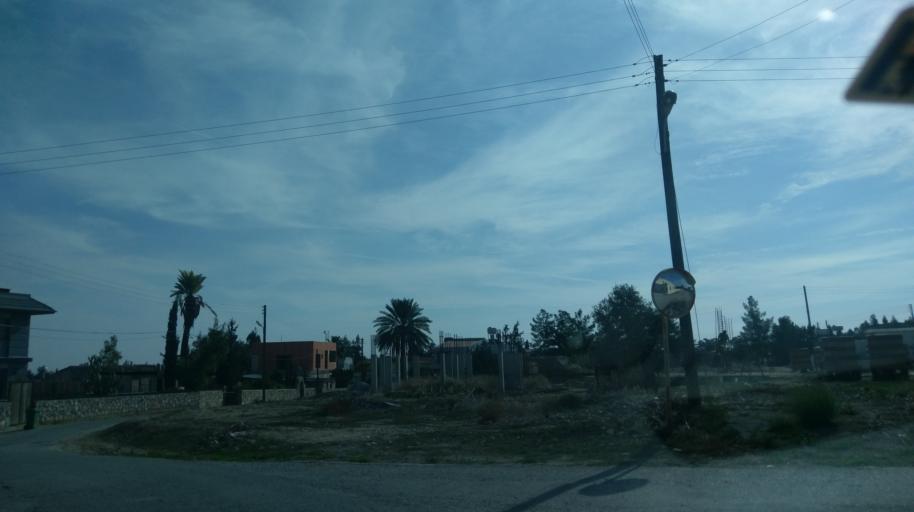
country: CY
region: Ammochostos
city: Lefkonoiko
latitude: 35.2190
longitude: 33.6977
